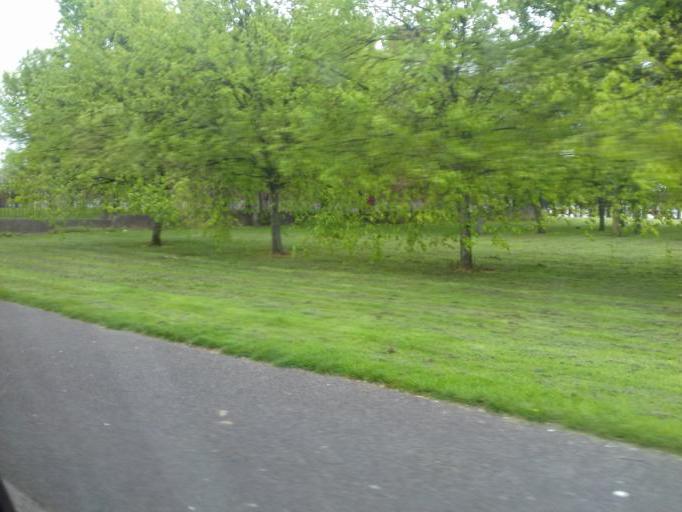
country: IE
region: Leinster
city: Crumlin
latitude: 53.3223
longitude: -6.3345
